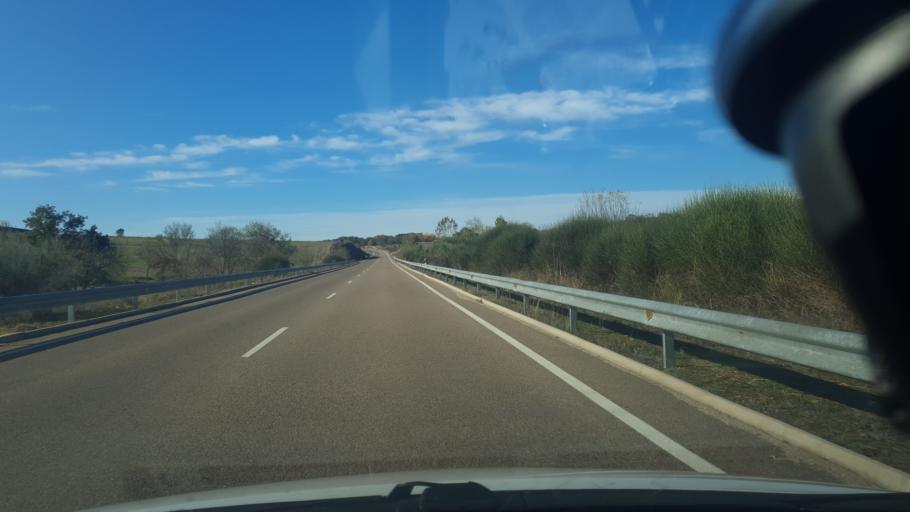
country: ES
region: Castille and Leon
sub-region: Provincia de Avila
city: Candeleda
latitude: 40.1391
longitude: -5.2108
